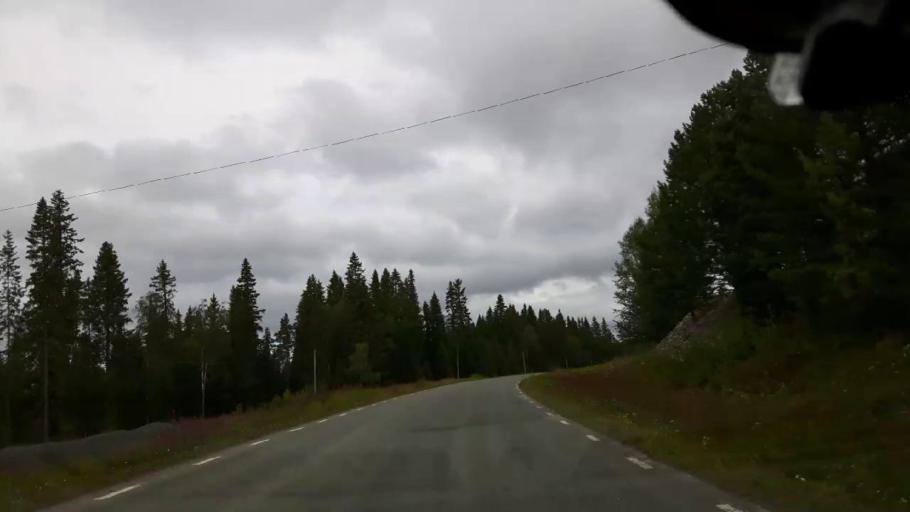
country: SE
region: Jaemtland
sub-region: Krokoms Kommun
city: Valla
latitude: 63.5138
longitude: 13.8788
